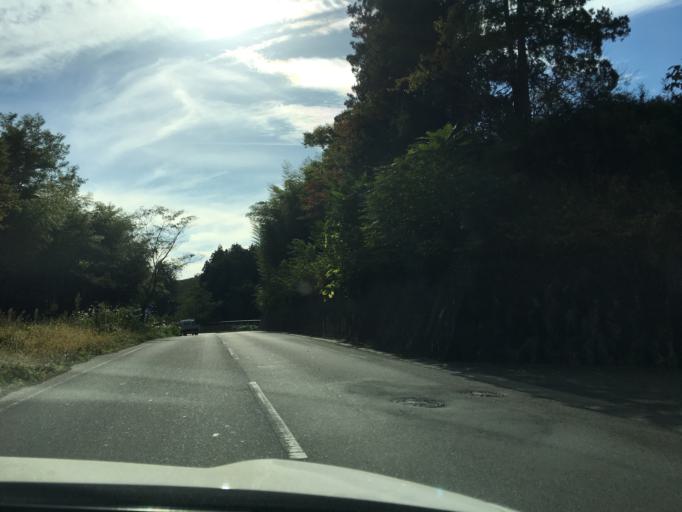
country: JP
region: Fukushima
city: Koriyama
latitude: 37.3743
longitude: 140.4454
